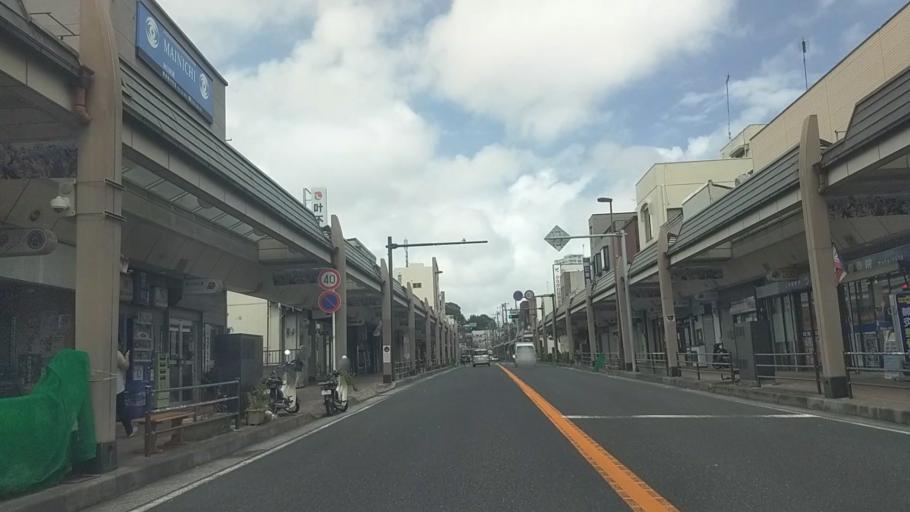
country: JP
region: Kanagawa
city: Yokosuka
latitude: 35.2728
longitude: 139.6704
